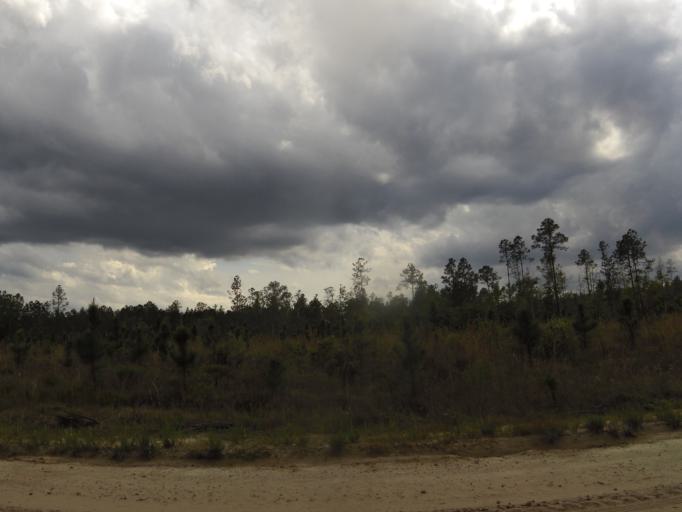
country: US
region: Georgia
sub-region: Charlton County
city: Folkston
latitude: 30.9408
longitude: -82.0148
